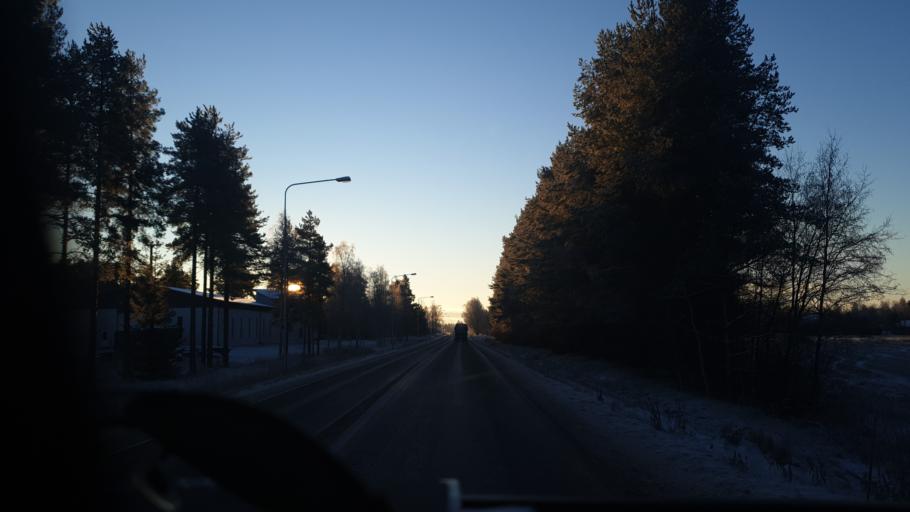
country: FI
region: Northern Ostrobothnia
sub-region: Ylivieska
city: Kalajoki
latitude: 64.2719
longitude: 23.9490
